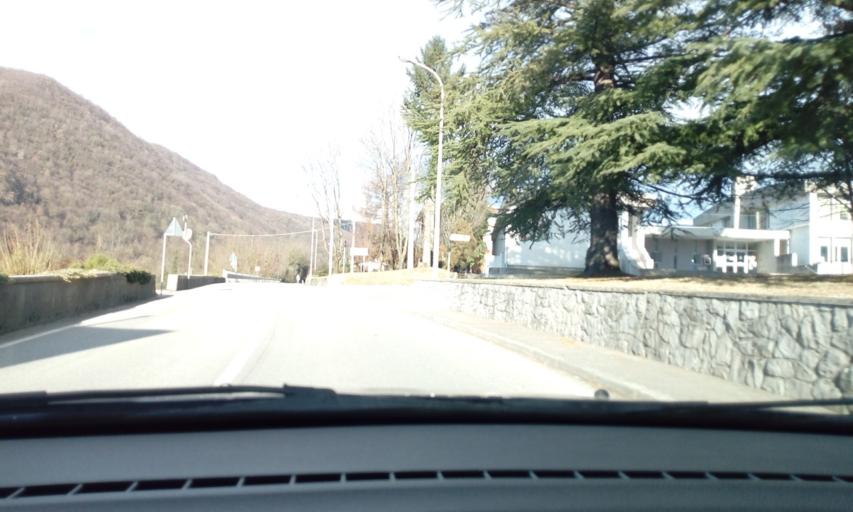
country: IT
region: Friuli Venezia Giulia
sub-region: Provincia di Udine
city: San Pietro al Natisone
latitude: 46.1303
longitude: 13.4863
